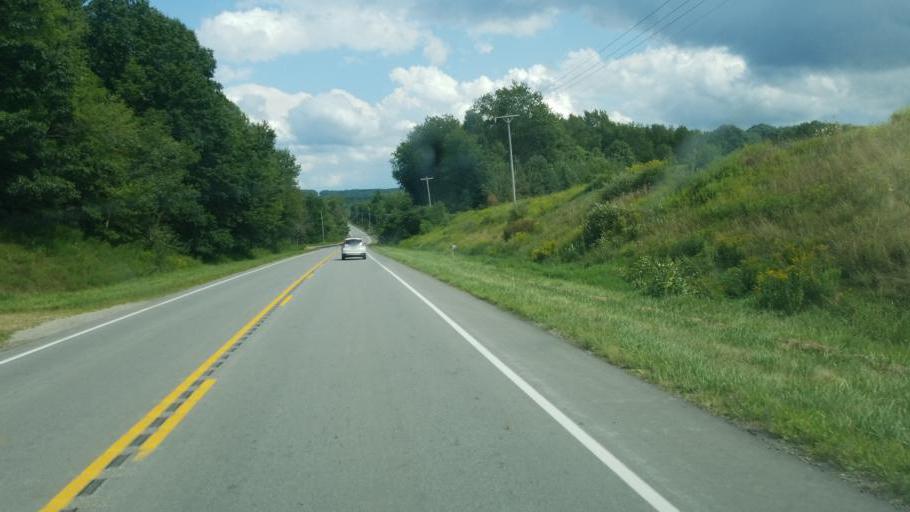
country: US
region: Pennsylvania
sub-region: Crawford County
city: Linesville
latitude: 41.6058
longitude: -80.4038
